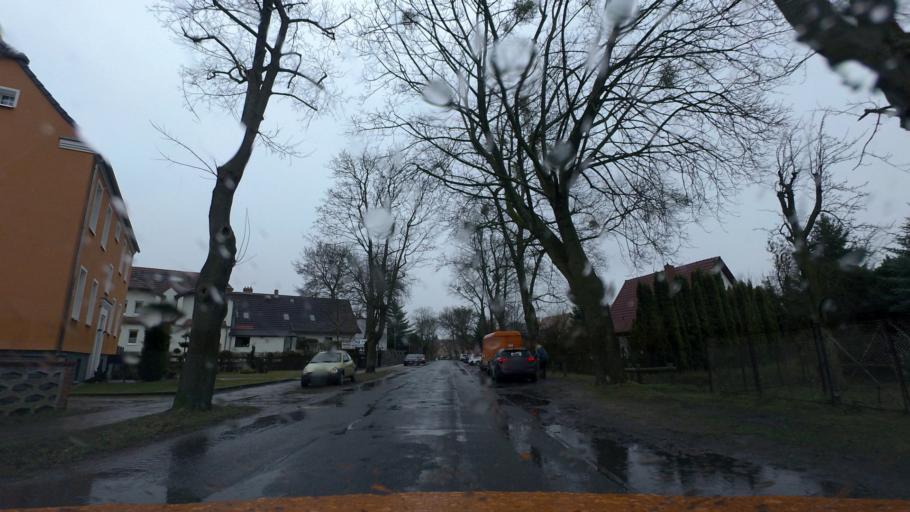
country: DE
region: Brandenburg
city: Brieselang
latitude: 52.5875
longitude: 13.0018
